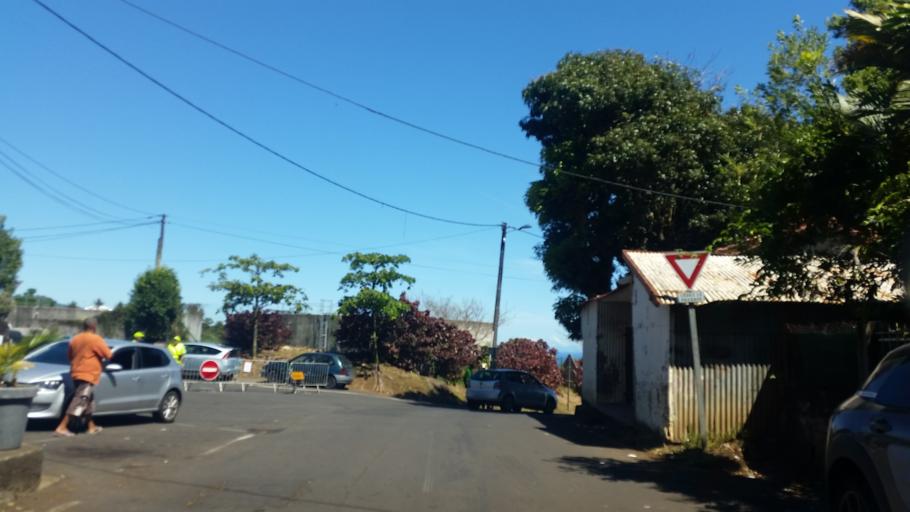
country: RE
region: Reunion
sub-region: Reunion
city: Sainte-Marie
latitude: -20.9304
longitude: 55.5311
